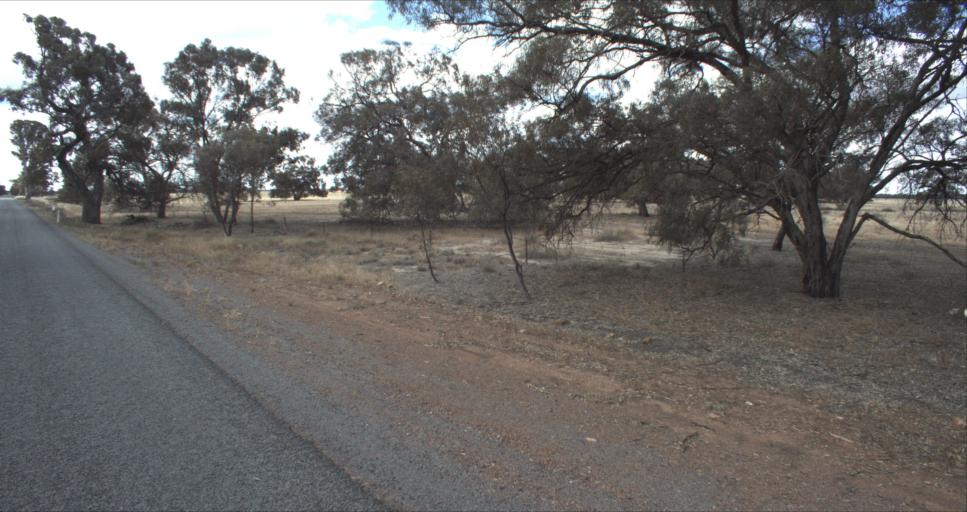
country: AU
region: New South Wales
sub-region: Leeton
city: Leeton
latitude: -34.6920
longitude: 146.3435
